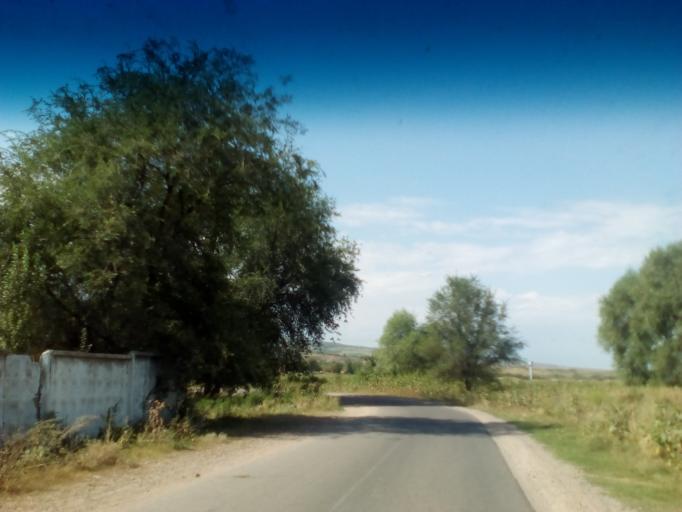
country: KZ
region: Almaty Oblysy
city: Burunday
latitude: 43.1636
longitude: 76.3820
